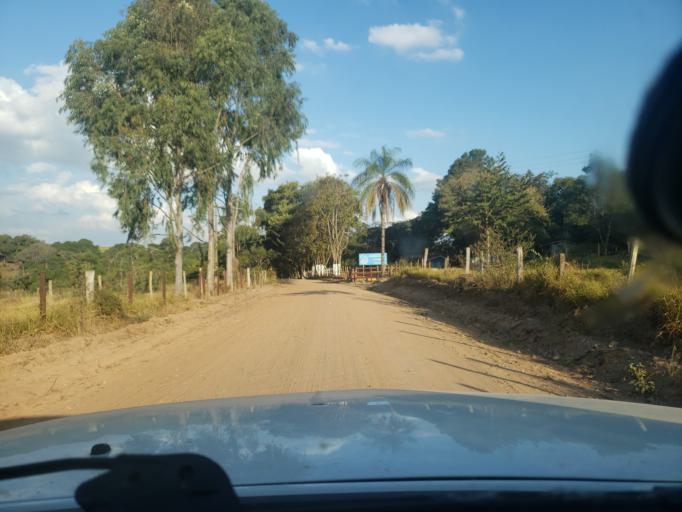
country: BR
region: Sao Paulo
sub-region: Mogi-Mirim
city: Mogi Mirim
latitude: -22.4583
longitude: -46.9401
